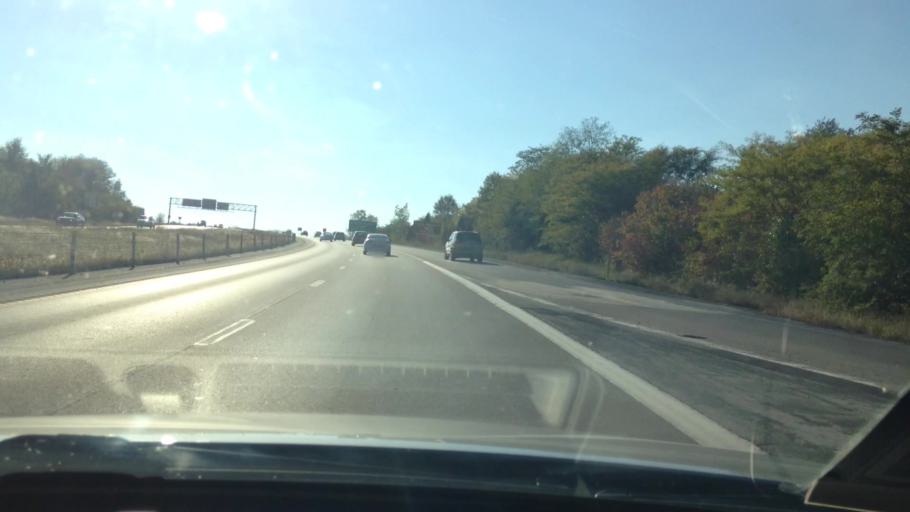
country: US
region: Missouri
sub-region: Clay County
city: Gladstone
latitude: 39.2598
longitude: -94.5930
